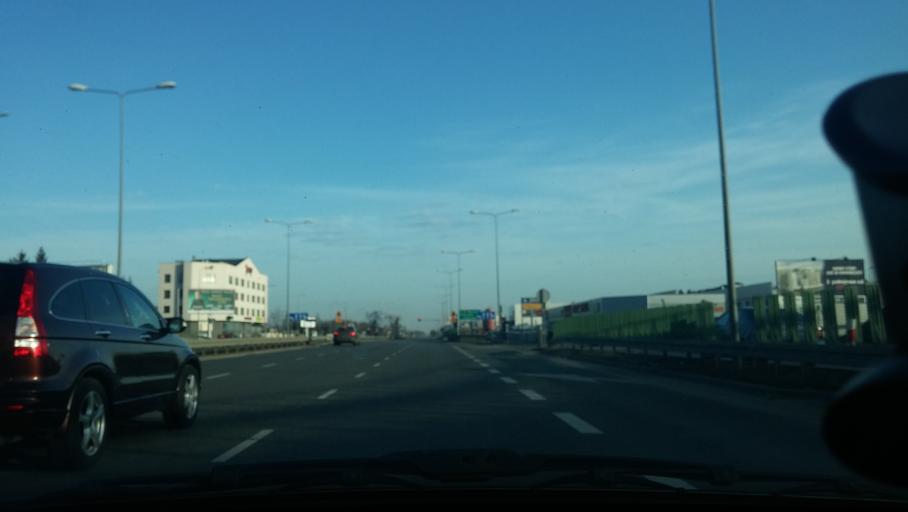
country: PL
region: Masovian Voivodeship
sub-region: Powiat piaseczynski
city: Mysiadlo
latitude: 52.0954
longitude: 21.0191
